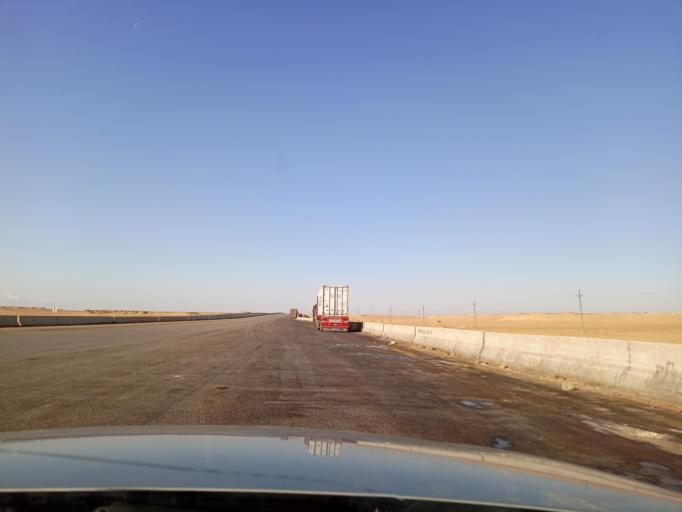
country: EG
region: Muhafazat al Fayyum
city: Tamiyah
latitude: 29.6382
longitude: 30.9875
